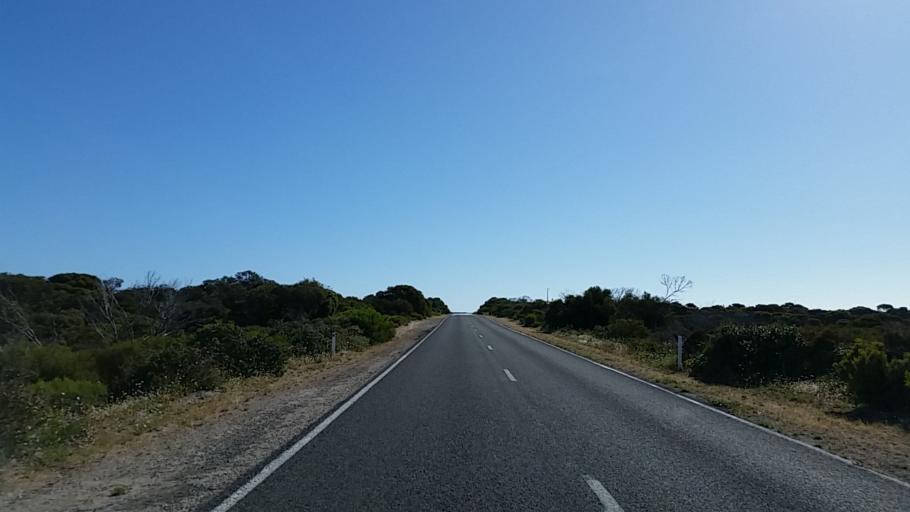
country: AU
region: South Australia
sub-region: Yorke Peninsula
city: Honiton
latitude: -35.2577
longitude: 136.9617
